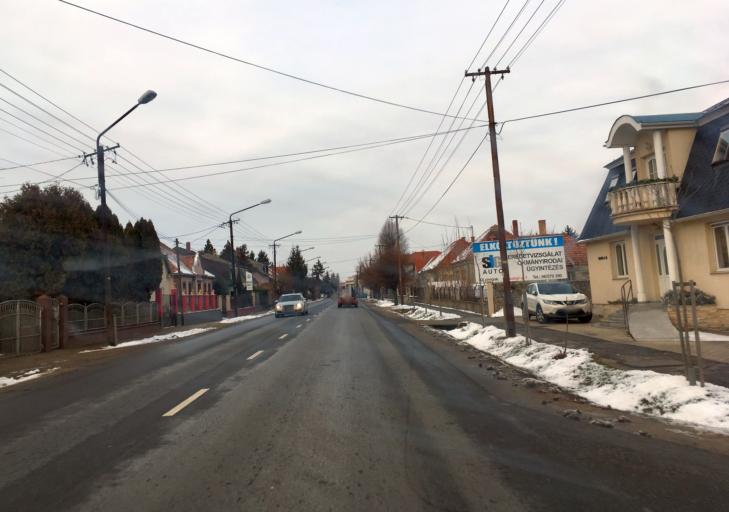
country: HU
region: Gyor-Moson-Sopron
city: Mosonmagyarovar
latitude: 47.8669
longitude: 17.2681
